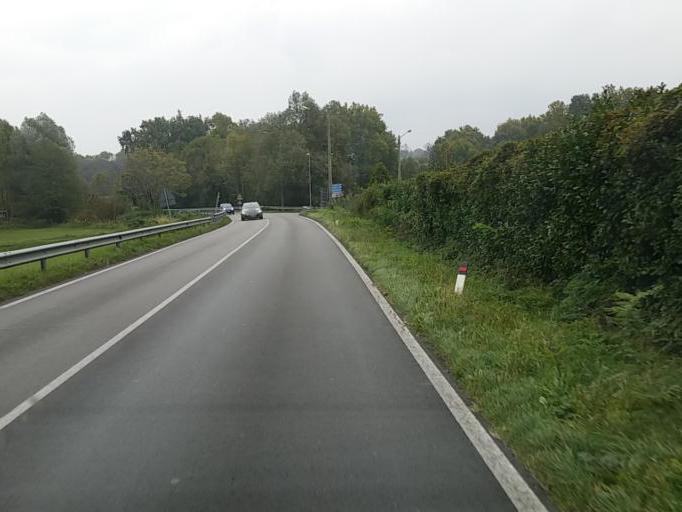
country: IT
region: Lombardy
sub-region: Provincia di Varese
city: Galliate Lombardo
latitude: 45.7885
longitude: 8.7803
